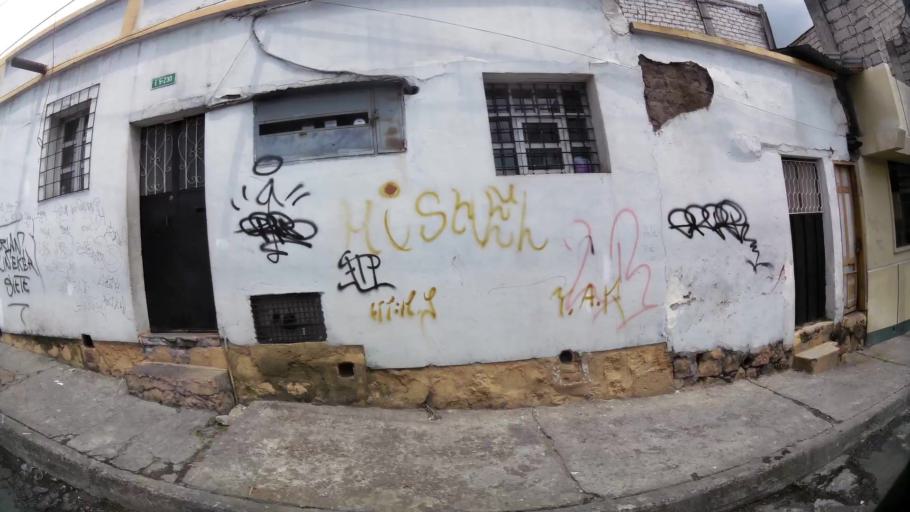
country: EC
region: Pichincha
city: Quito
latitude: -0.2572
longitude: -78.5158
